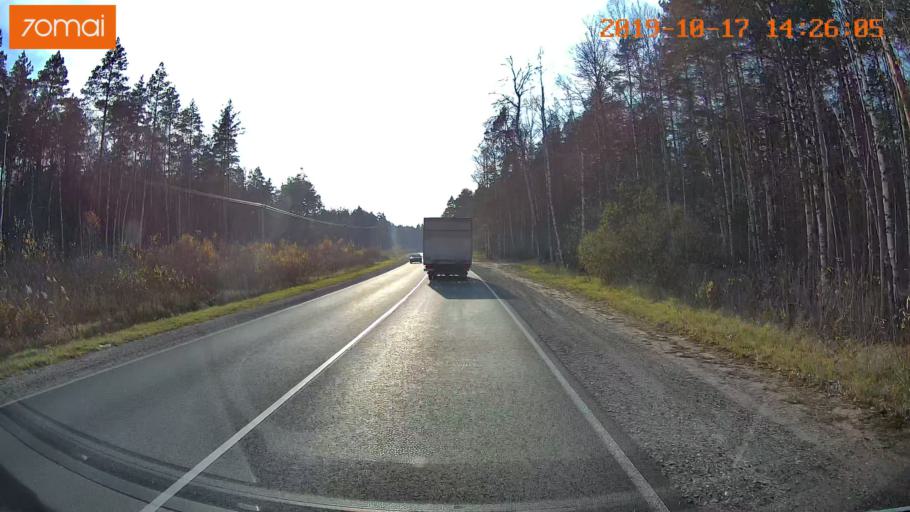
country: RU
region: Moskovskaya
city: Radovitskiy
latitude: 54.9950
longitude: 39.9717
